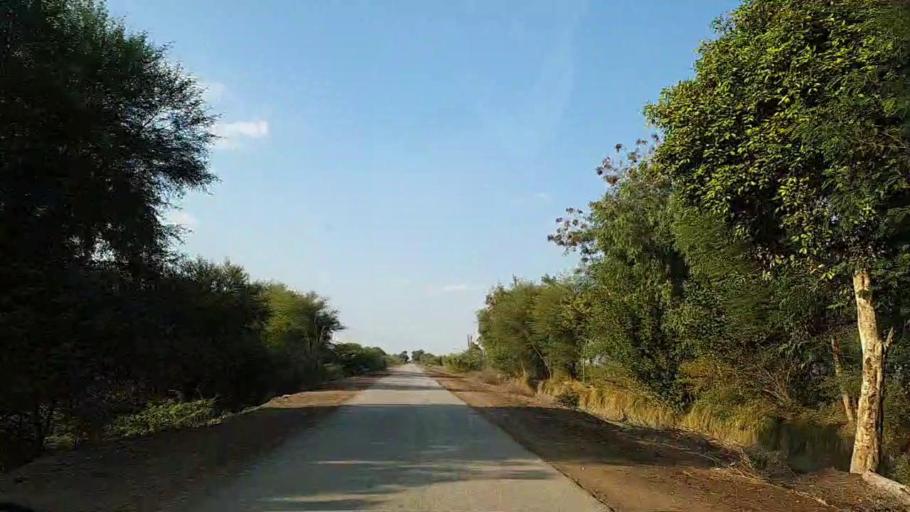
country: PK
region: Sindh
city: Tando Mittha Khan
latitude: 25.7280
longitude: 69.2136
